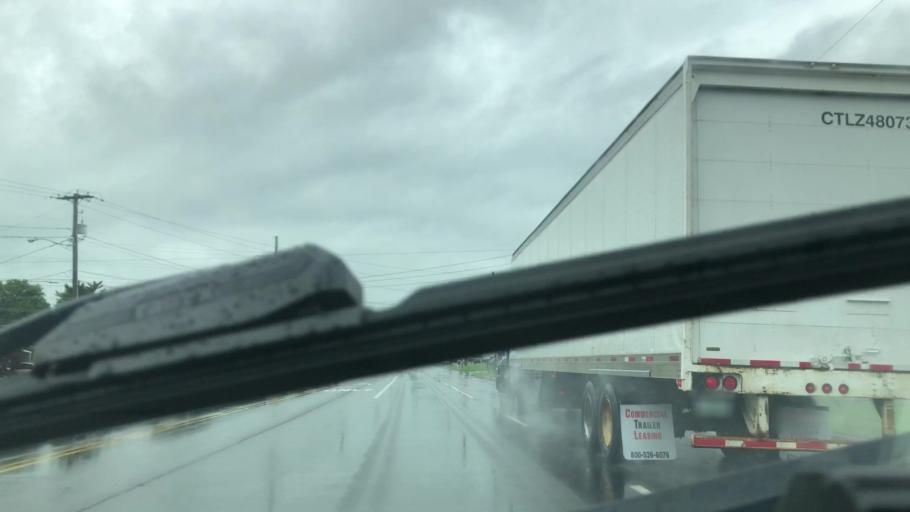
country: US
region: Pennsylvania
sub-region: Lehigh County
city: Trexlertown
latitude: 40.5894
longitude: -75.6027
